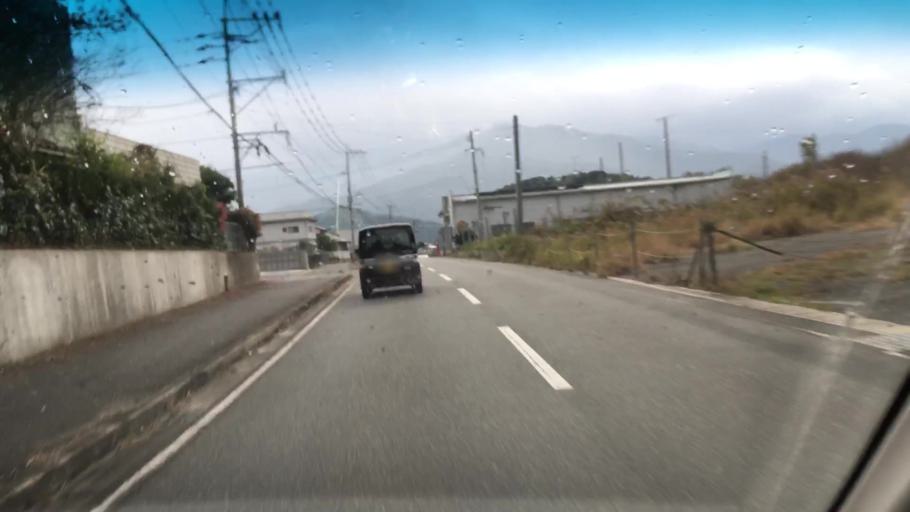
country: JP
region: Fukuoka
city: Maebaru-chuo
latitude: 33.5290
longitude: 130.1968
